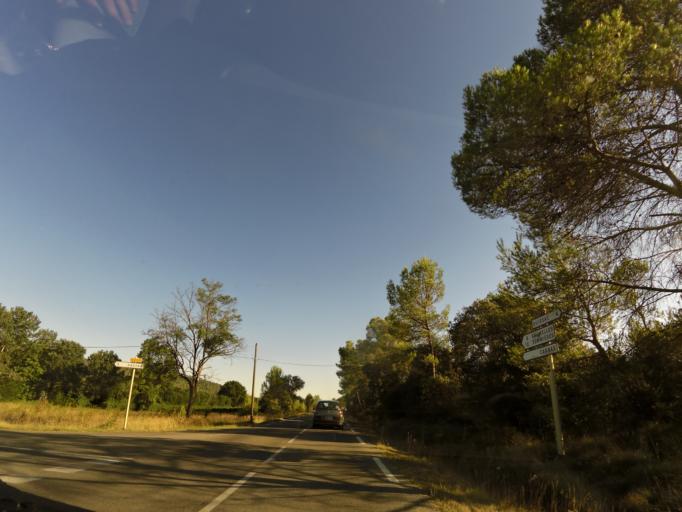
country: FR
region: Languedoc-Roussillon
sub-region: Departement du Gard
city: Quissac
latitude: 43.8605
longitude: 4.0170
